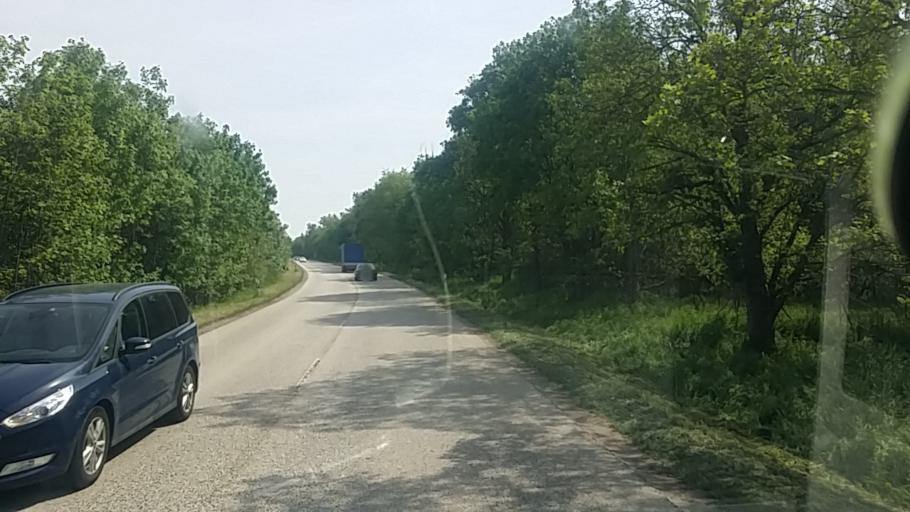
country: HU
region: Fejer
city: Etyek
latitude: 47.4963
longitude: 18.7610
